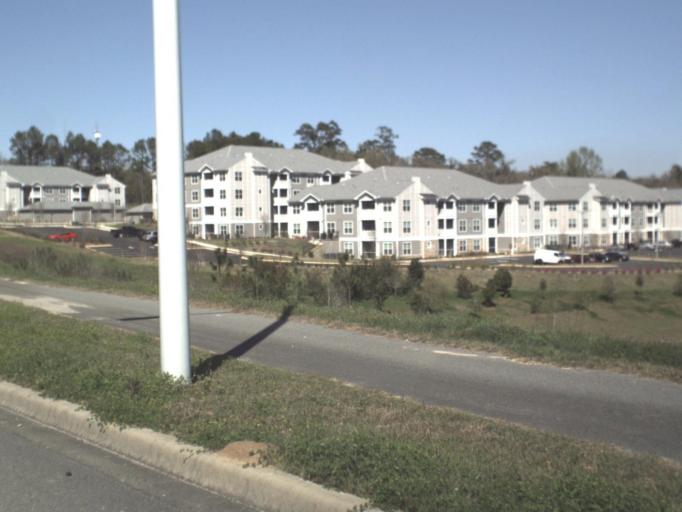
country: US
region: Florida
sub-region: Leon County
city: Tallahassee
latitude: 30.4131
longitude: -84.2347
